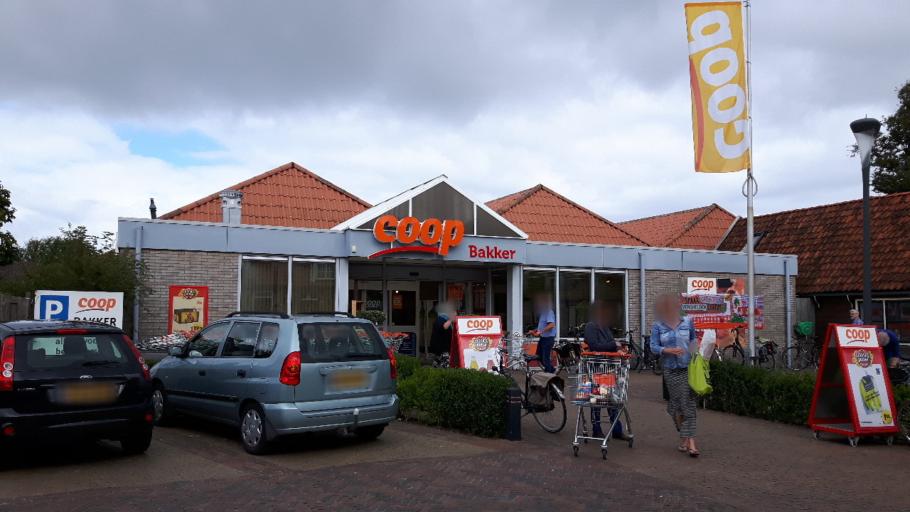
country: NL
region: Friesland
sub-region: Gemeente Ameland
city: Hollum
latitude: 53.4411
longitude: 5.6366
